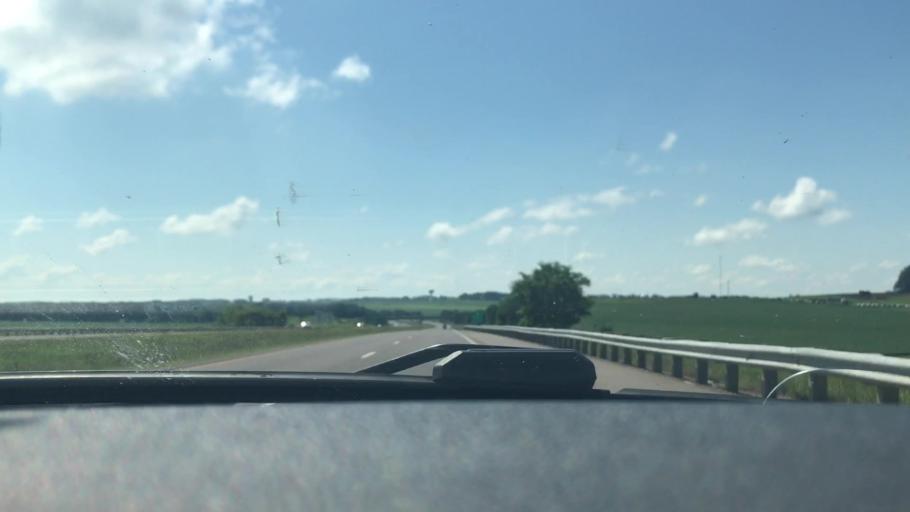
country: US
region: Wisconsin
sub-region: Chippewa County
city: Bloomer
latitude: 45.1181
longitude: -91.5201
